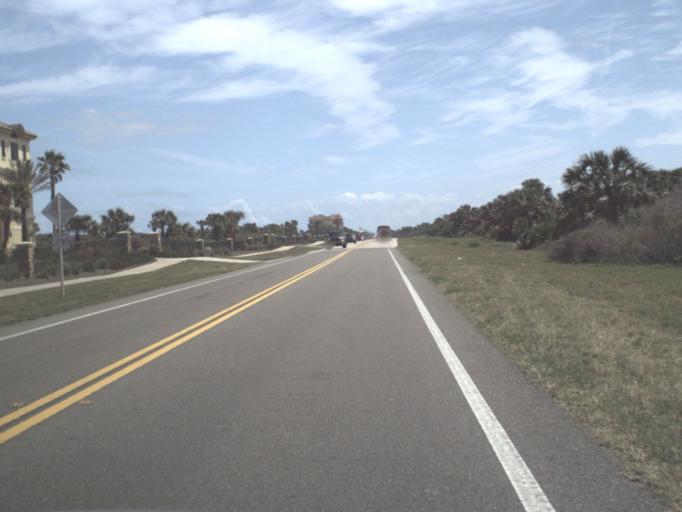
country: US
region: Florida
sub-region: Flagler County
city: Palm Coast
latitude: 29.5597
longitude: -81.1668
